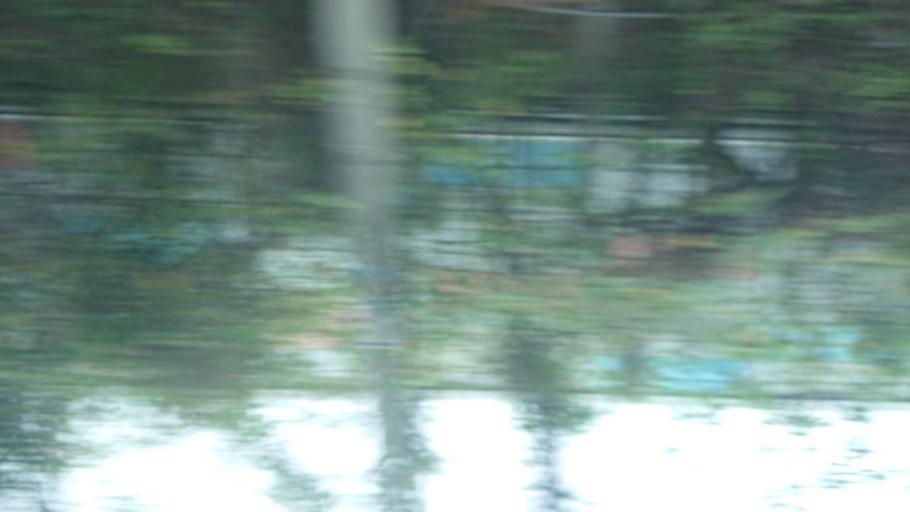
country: TW
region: Taiwan
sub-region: Hsinchu
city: Hsinchu
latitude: 24.8329
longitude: 120.9530
